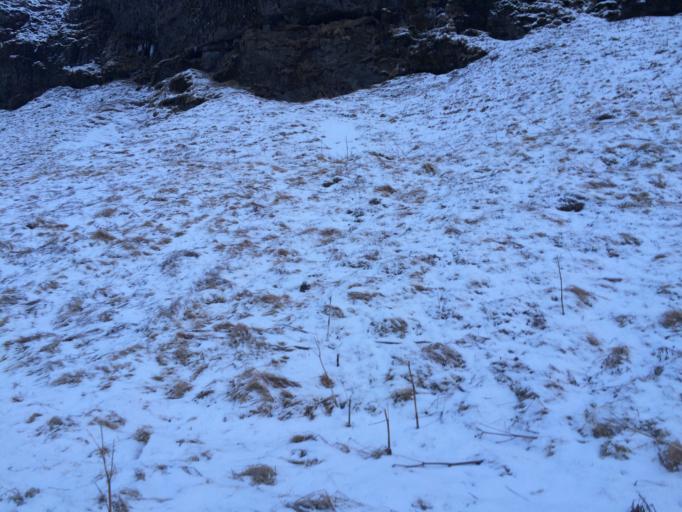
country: IS
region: South
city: Vestmannaeyjar
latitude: 63.6173
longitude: -19.9887
